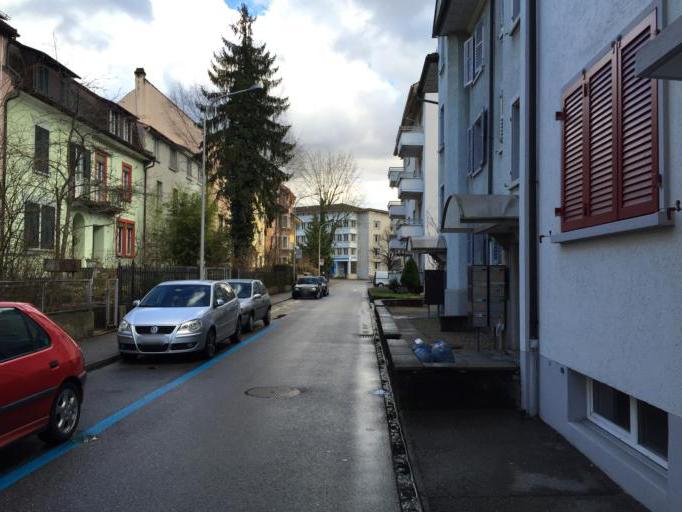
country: CH
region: Solothurn
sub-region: Bezirk Olten
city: Olten
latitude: 47.3522
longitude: 7.9089
